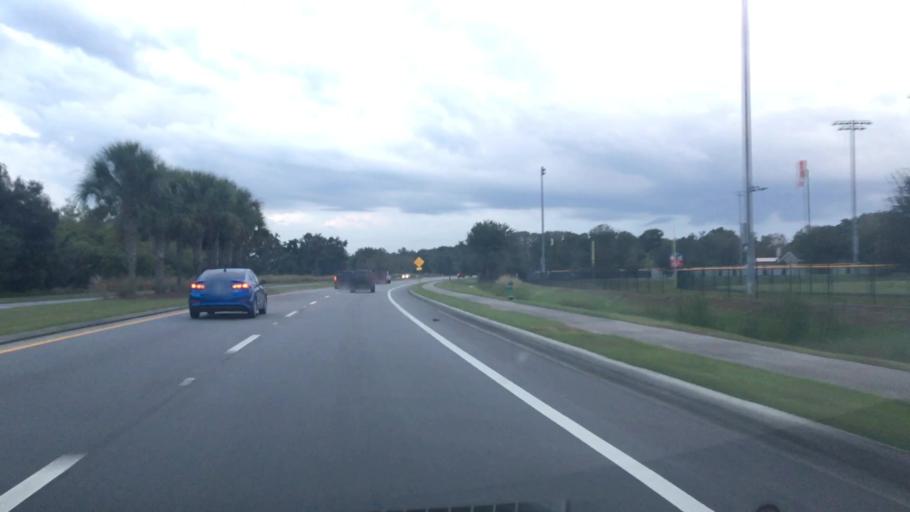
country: US
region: Florida
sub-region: Seminole County
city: Midway
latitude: 28.7613
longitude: -81.2170
